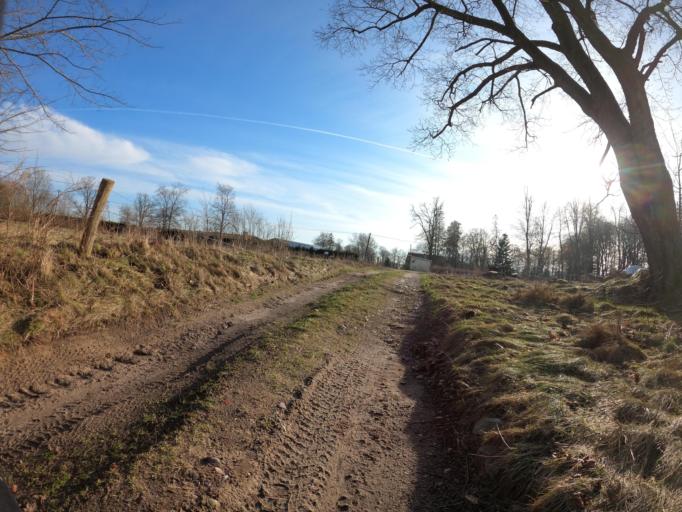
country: PL
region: West Pomeranian Voivodeship
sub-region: Powiat koszalinski
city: Polanow
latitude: 54.2022
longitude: 16.6535
